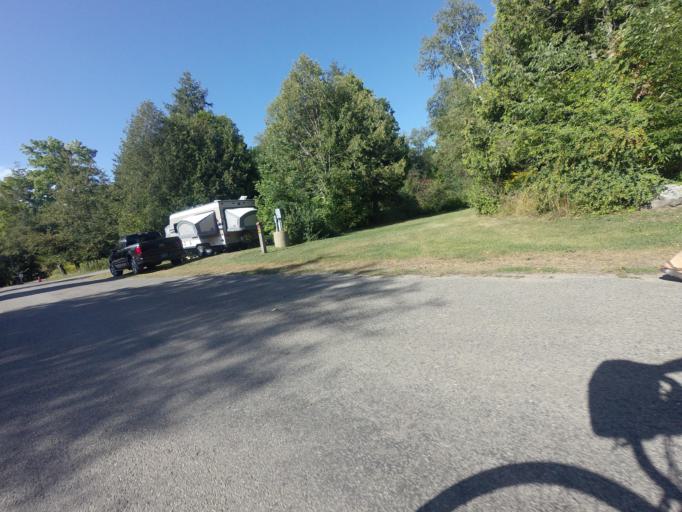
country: CA
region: Ontario
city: Waterloo
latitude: 43.6646
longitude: -80.4500
